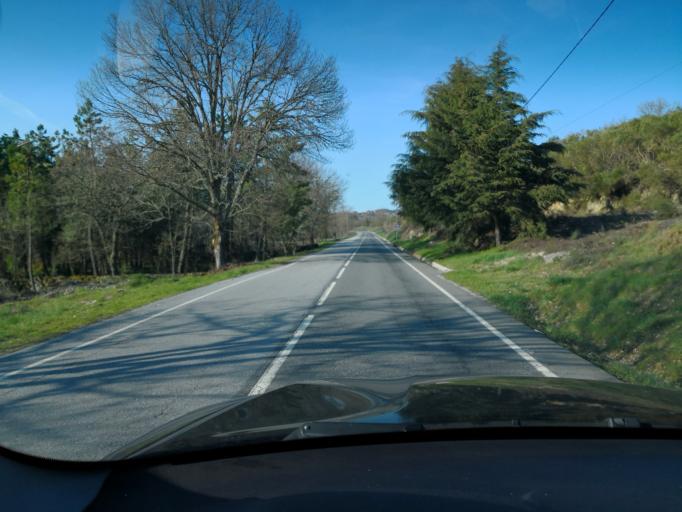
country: PT
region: Vila Real
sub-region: Sabrosa
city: Sabrosa
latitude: 41.3577
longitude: -7.6441
